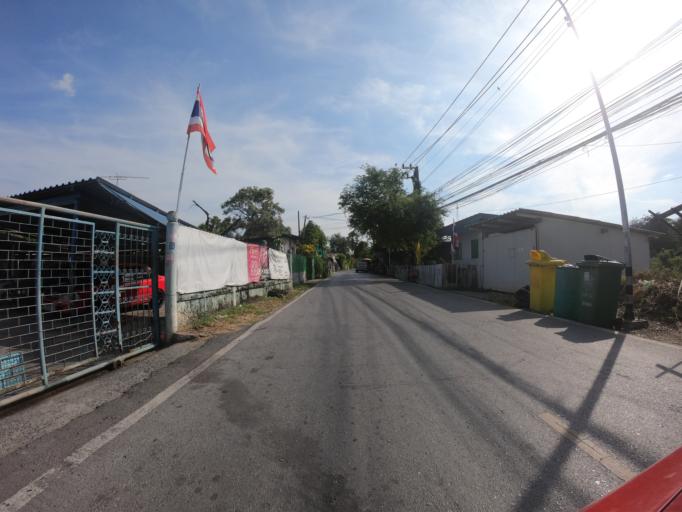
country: TH
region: Pathum Thani
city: Thanyaburi
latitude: 14.0164
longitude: 100.7325
